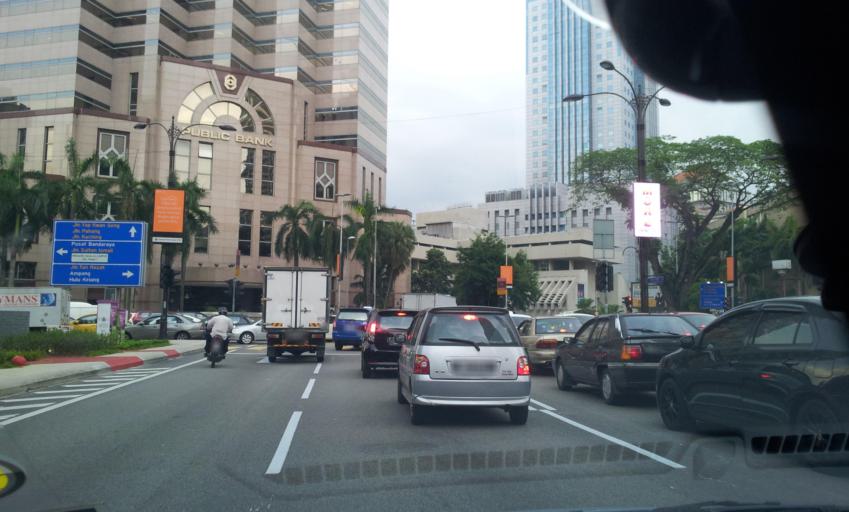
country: MY
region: Kuala Lumpur
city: Kuala Lumpur
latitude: 3.1589
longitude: 101.7104
